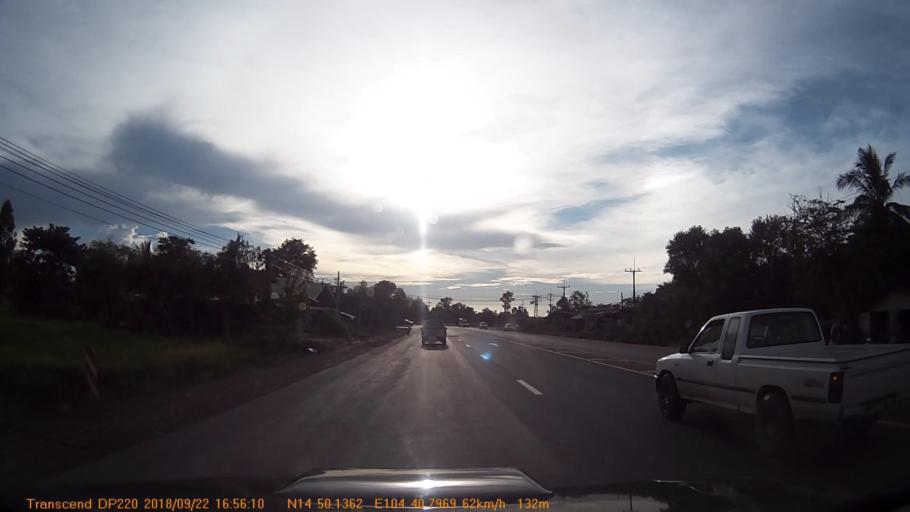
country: TH
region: Sisaket
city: Benchalak
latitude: 14.8356
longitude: 104.6800
